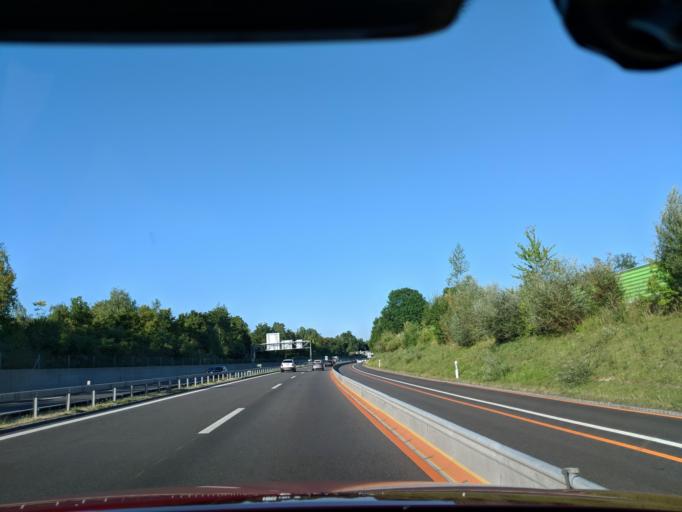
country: CH
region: Saint Gallen
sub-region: Wahlkreis St. Gallen
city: Andwil
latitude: 47.4157
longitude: 9.3186
